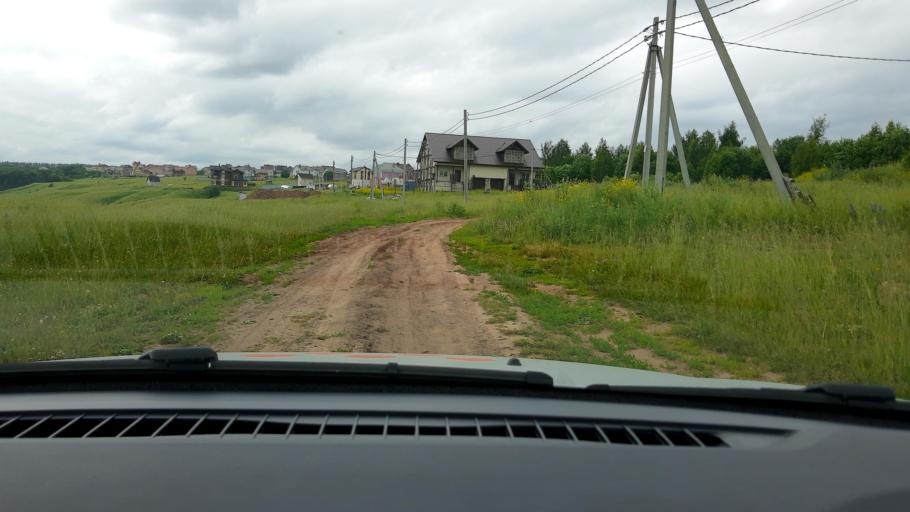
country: RU
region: Nizjnij Novgorod
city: Nizhniy Novgorod
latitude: 56.2258
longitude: 43.9859
